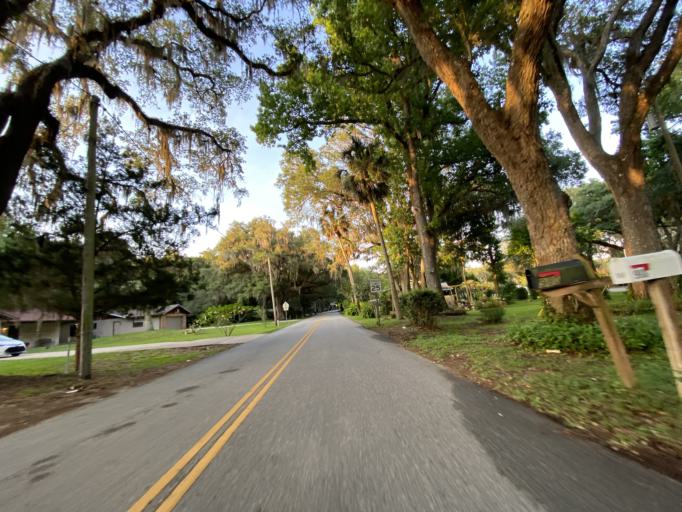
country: US
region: Florida
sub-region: Volusia County
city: Port Orange
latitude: 29.1398
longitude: -81.0072
